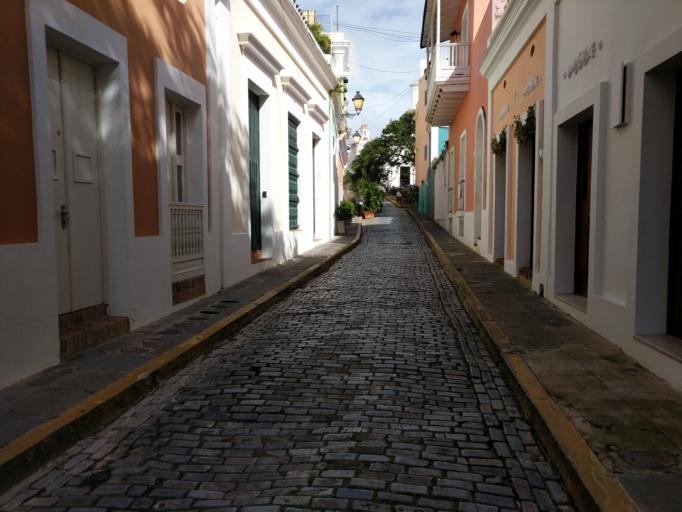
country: PR
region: San Juan
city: San Juan
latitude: 18.4656
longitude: -66.1191
